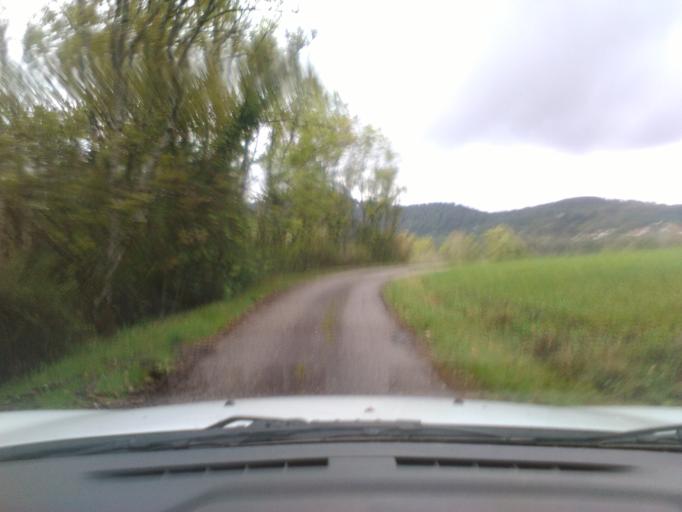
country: FR
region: Lorraine
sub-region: Departement des Vosges
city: Saint-Die-des-Vosges
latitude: 48.3058
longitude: 6.9728
